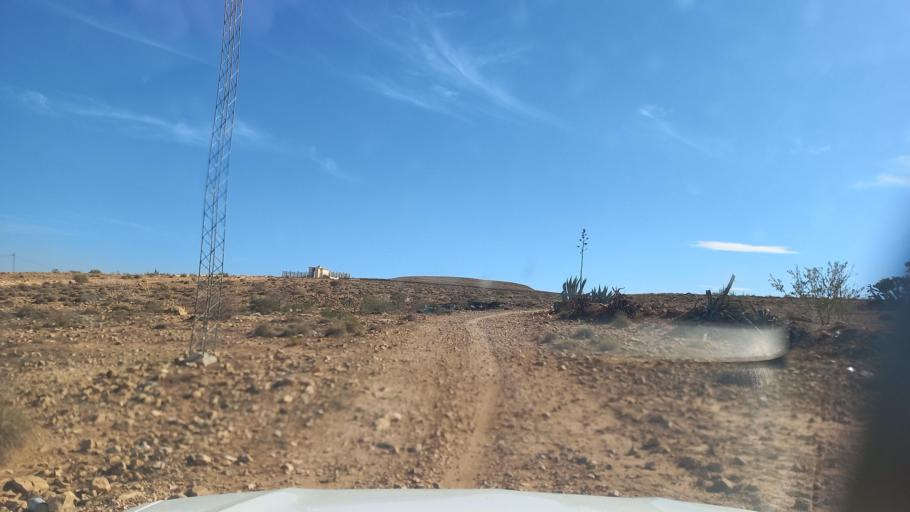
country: TN
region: Al Qasrayn
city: Kasserine
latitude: 35.2066
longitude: 8.9759
